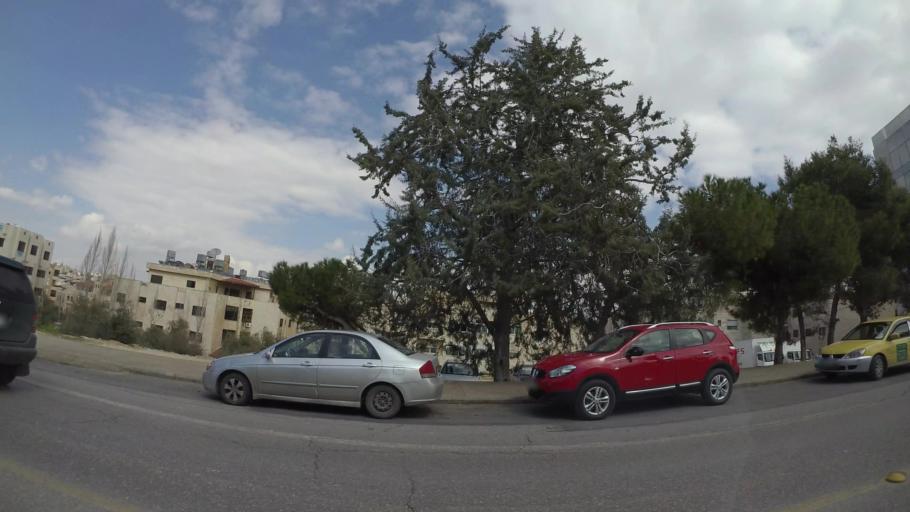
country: JO
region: Amman
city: Amman
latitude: 31.9766
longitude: 35.8971
